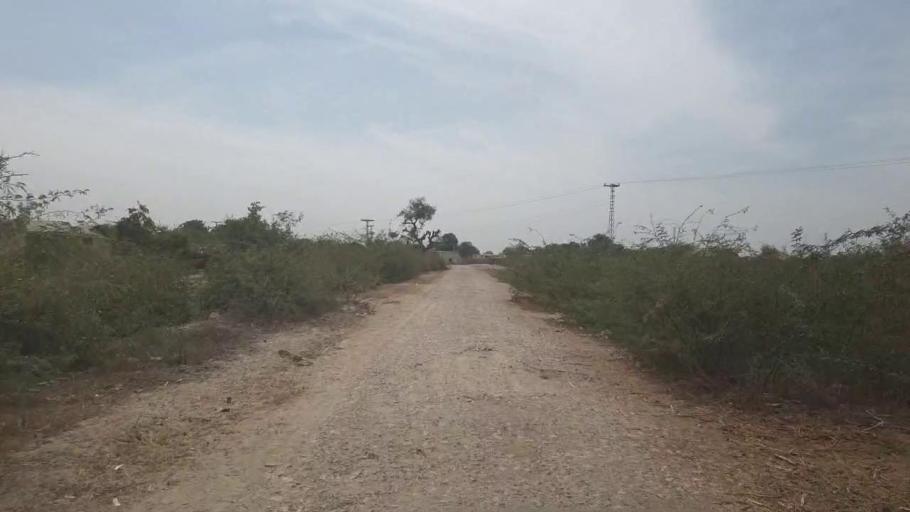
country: PK
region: Sindh
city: Kunri
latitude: 25.2264
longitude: 69.6844
